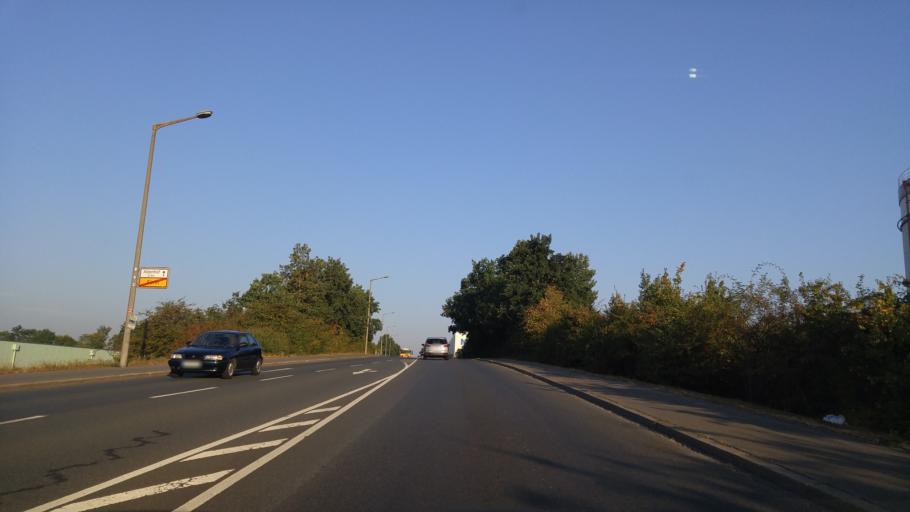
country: DE
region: Bavaria
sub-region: Regierungsbezirk Mittelfranken
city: Furth
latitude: 49.4964
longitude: 10.9493
